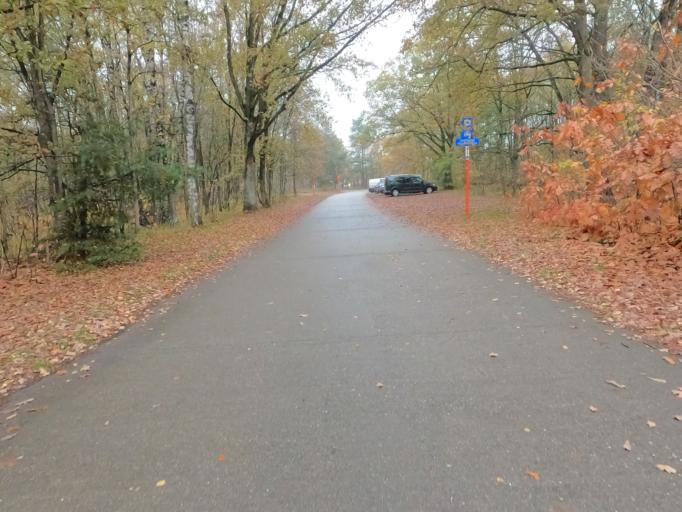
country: BE
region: Flanders
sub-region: Provincie Antwerpen
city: Nijlen
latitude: 51.1575
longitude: 4.6362
